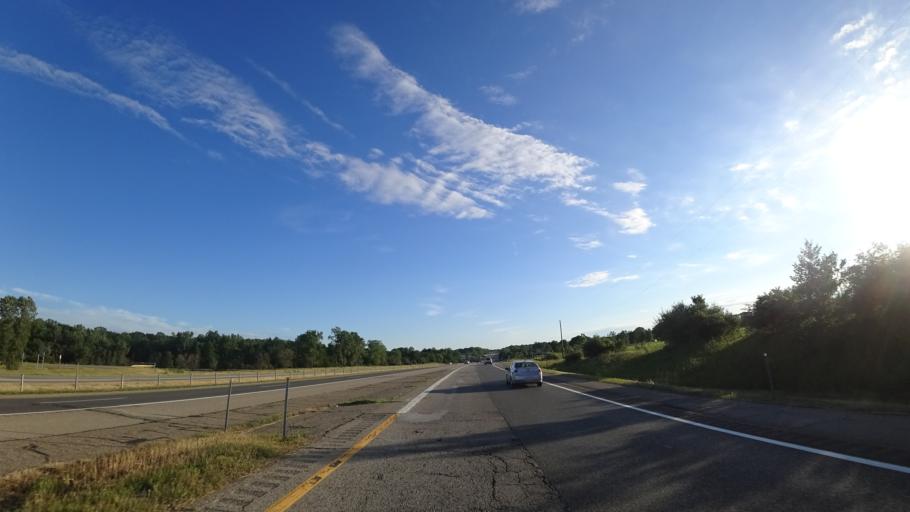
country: US
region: Michigan
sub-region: Berrien County
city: Benton Heights
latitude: 42.1322
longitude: -86.3719
